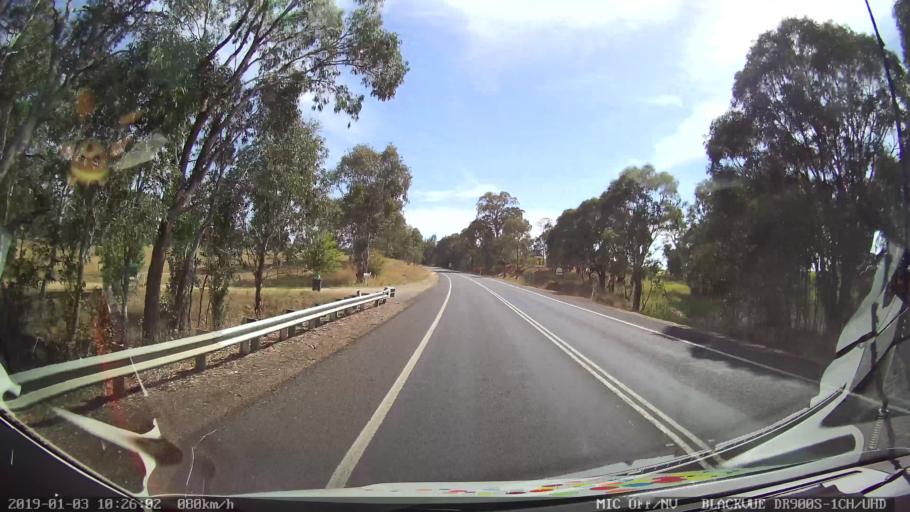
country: AU
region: New South Wales
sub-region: Young
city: Young
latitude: -34.4172
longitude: 148.2467
